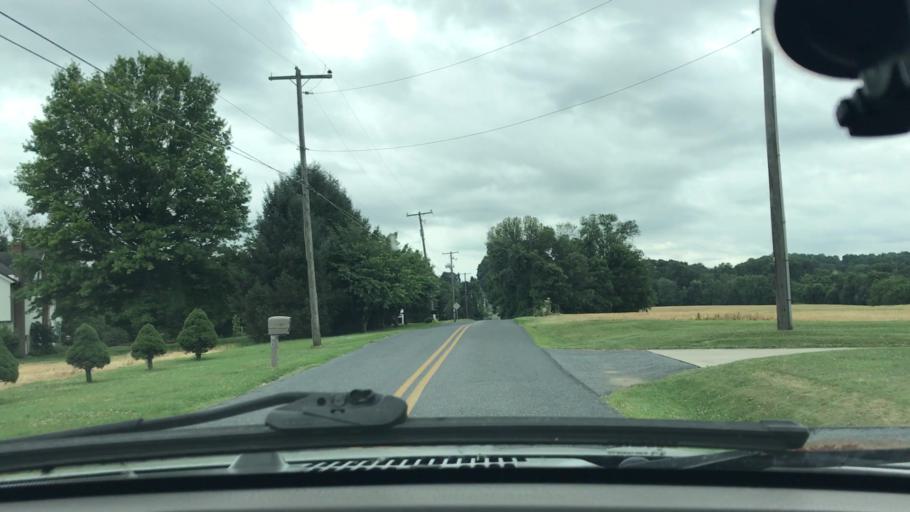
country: US
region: Pennsylvania
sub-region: Lancaster County
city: Elizabethtown
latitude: 40.1777
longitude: -76.6061
